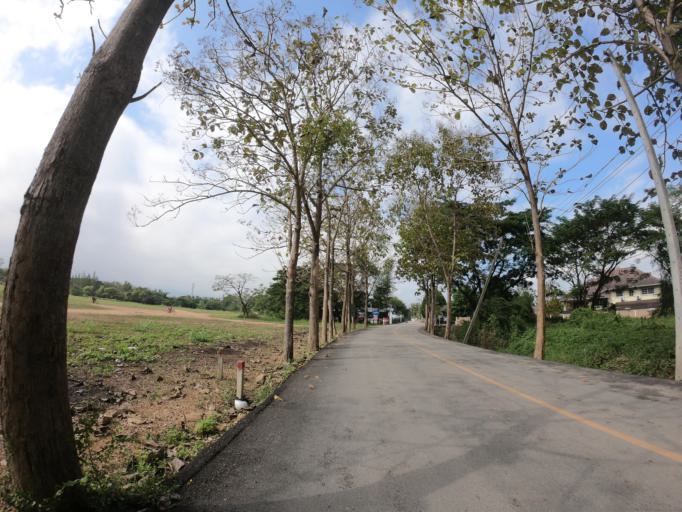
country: TH
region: Chiang Mai
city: San Sai
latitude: 18.8617
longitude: 99.0265
